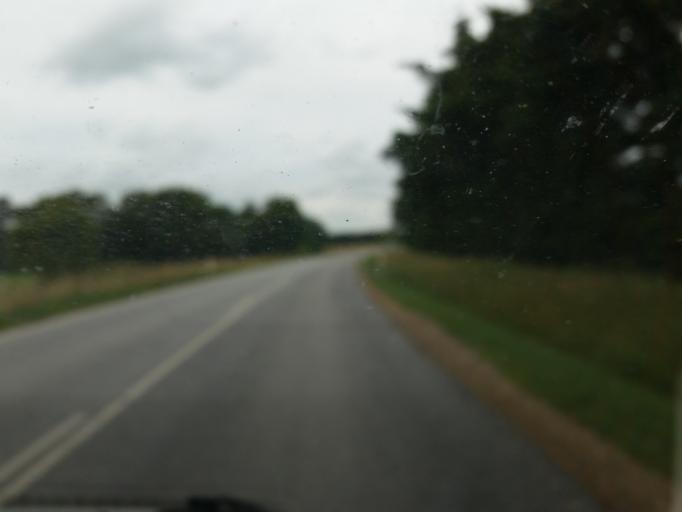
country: DK
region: South Denmark
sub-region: Esbjerg Kommune
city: Ribe
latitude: 55.3772
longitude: 8.8246
